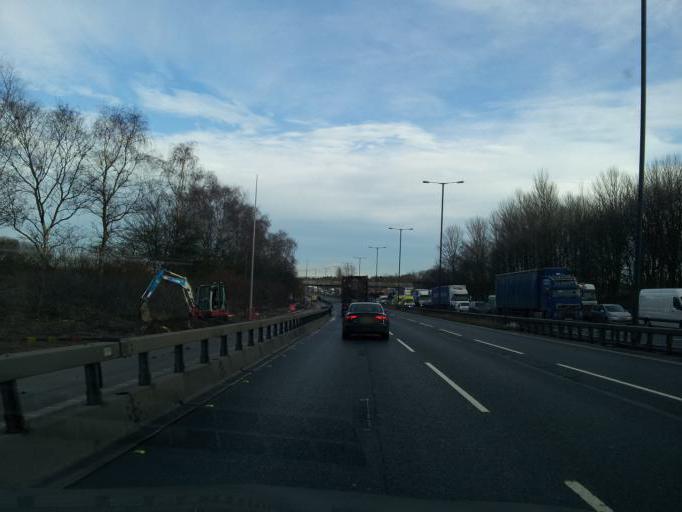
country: GB
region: England
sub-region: Manchester
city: Heywood
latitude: 53.5839
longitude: -2.1841
